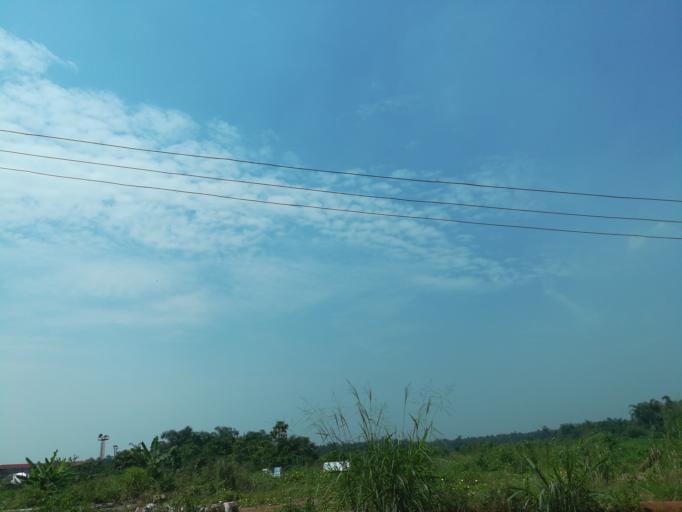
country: NG
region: Lagos
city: Ikorodu
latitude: 6.6626
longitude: 3.4683
